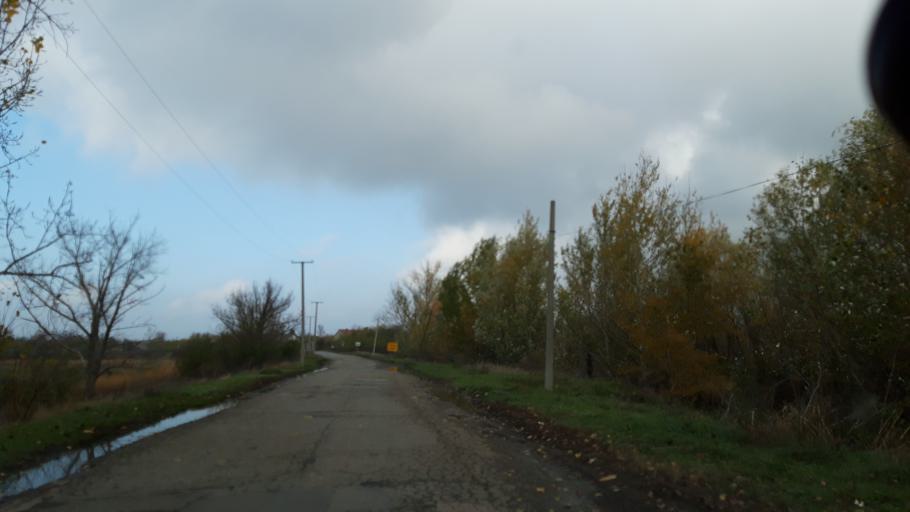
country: RS
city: Padej
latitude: 45.8180
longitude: 20.1587
